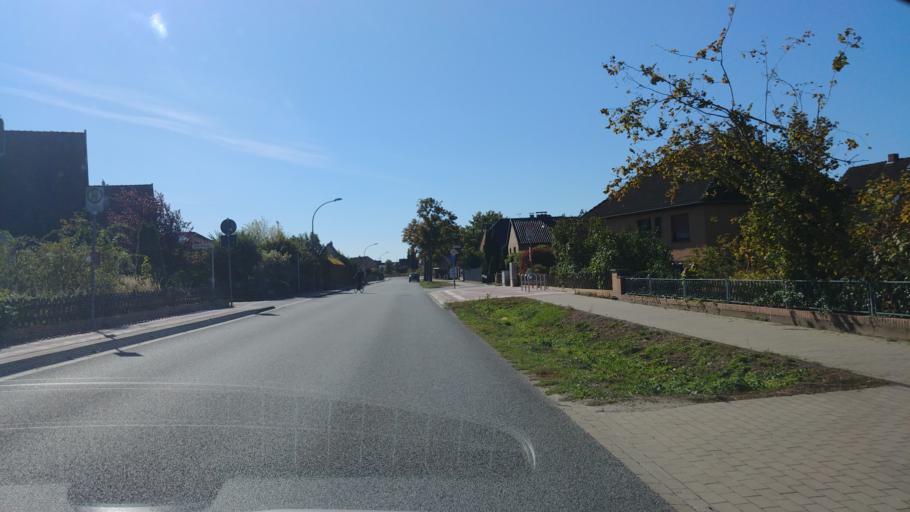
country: DE
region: Lower Saxony
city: Meinersen
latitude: 52.4774
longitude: 10.3626
